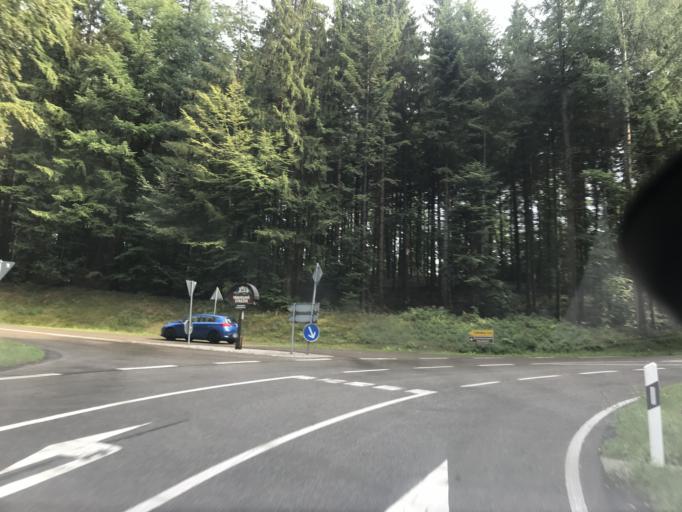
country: DE
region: Baden-Wuerttemberg
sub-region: Freiburg Region
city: Kandern
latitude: 47.7031
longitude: 7.7058
